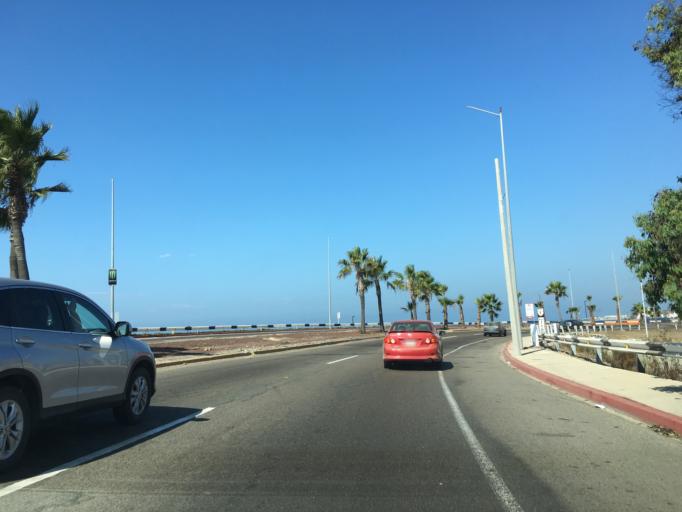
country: MX
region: Baja California
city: Ensenada
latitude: 31.8583
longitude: -116.6359
